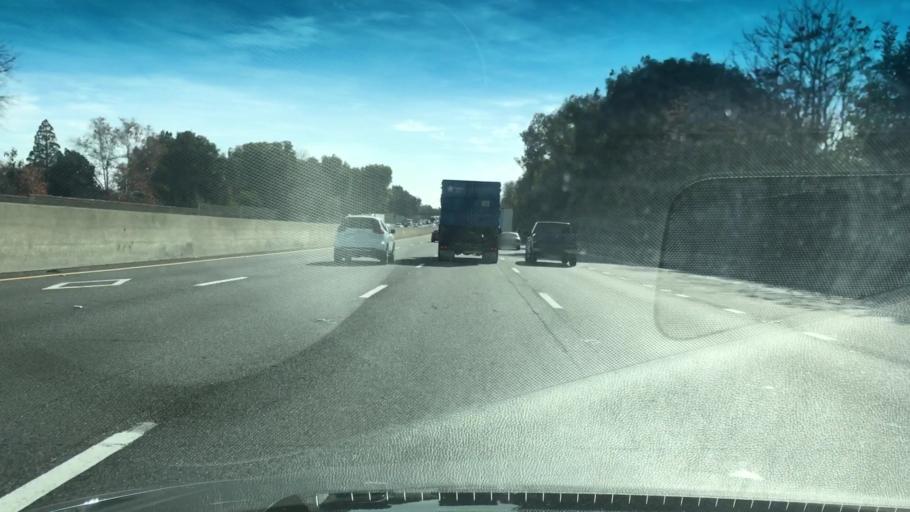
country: US
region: California
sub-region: Sacramento County
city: Parkway
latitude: 38.5326
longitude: -121.4719
